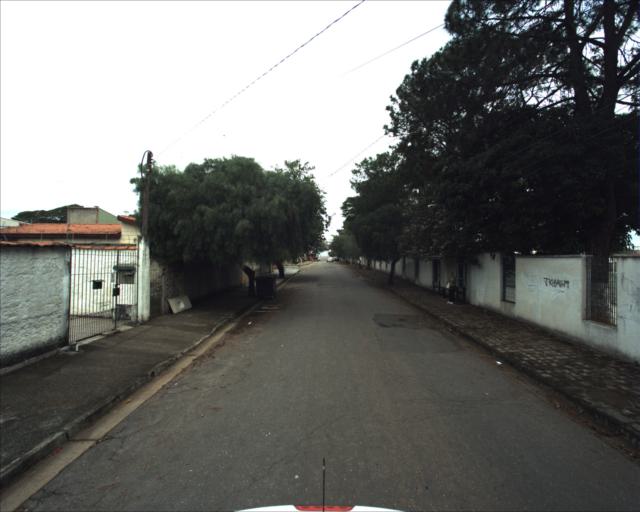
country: BR
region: Sao Paulo
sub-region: Sorocaba
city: Sorocaba
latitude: -23.5028
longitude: -47.4945
